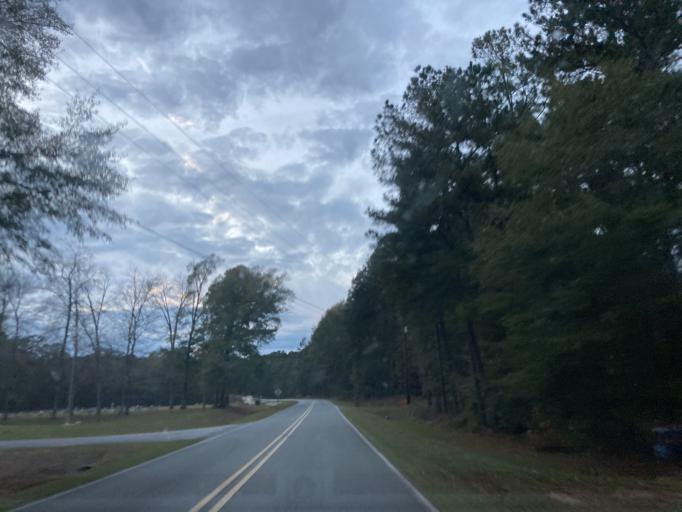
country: US
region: Georgia
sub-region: Jones County
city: Gray
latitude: 32.9737
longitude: -83.5101
